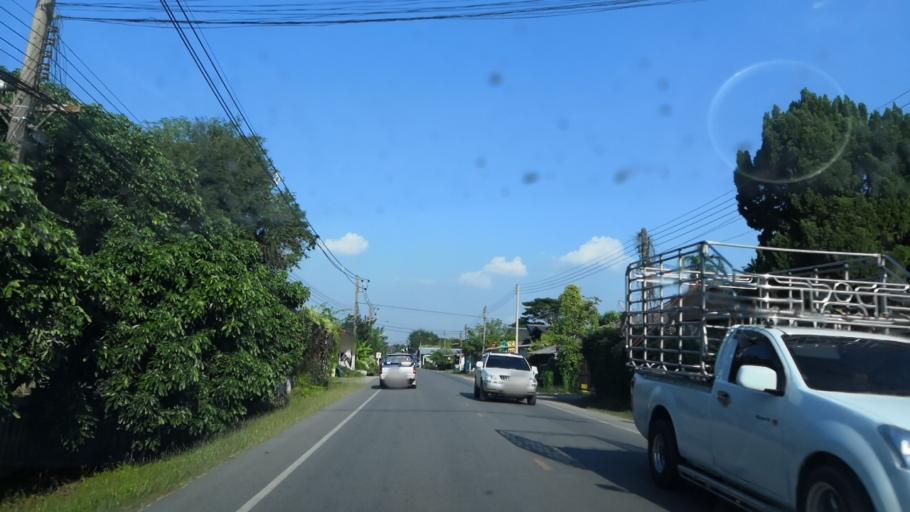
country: TH
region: Chiang Rai
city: Wiang Chai
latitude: 19.9341
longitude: 99.9025
